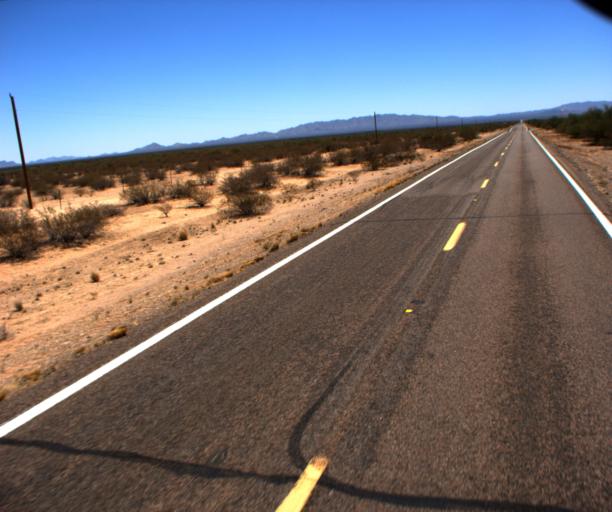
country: US
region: Arizona
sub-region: Pima County
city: Ajo
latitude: 32.1969
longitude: -112.4671
